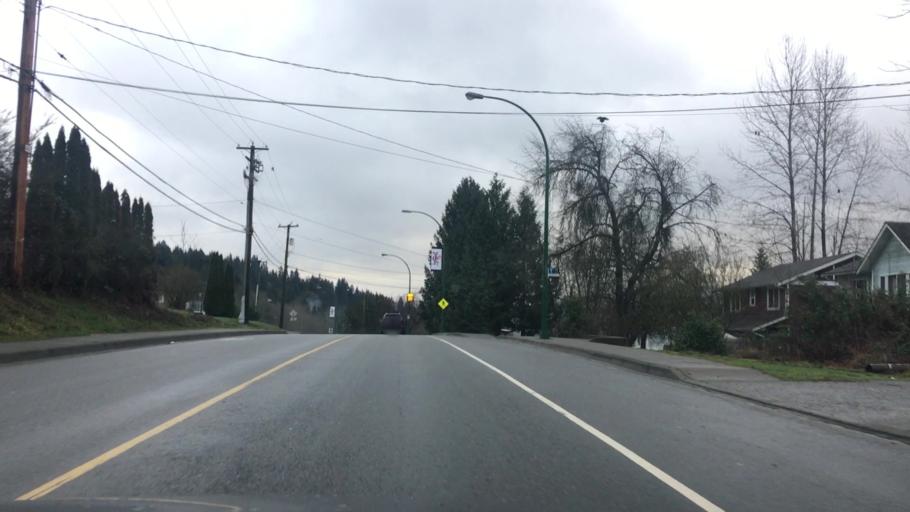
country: CA
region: British Columbia
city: Burnaby
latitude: 49.3086
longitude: -122.9904
